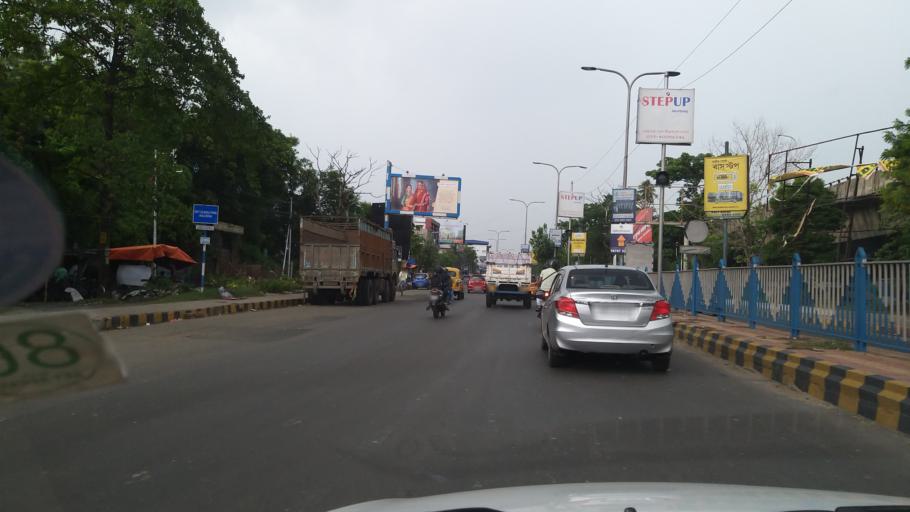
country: IN
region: West Bengal
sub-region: North 24 Parganas
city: Dam Dam
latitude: 22.6538
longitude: 88.4390
